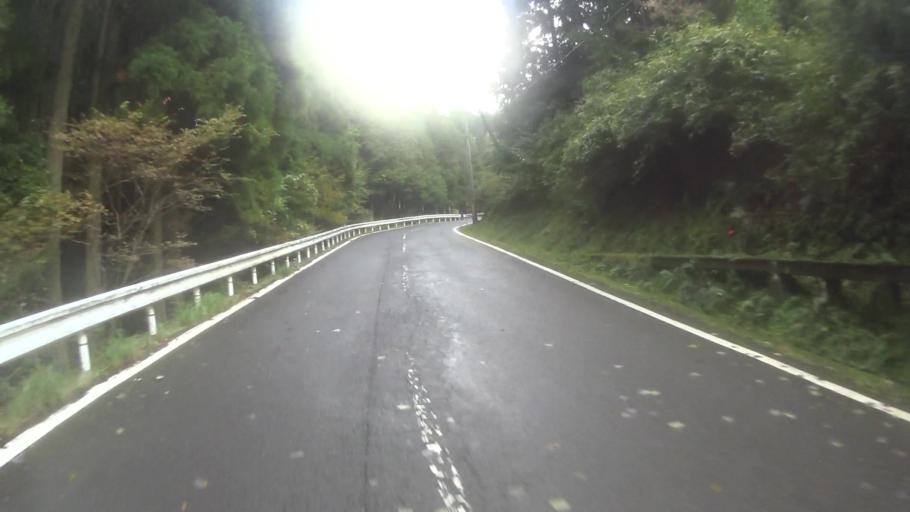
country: JP
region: Kyoto
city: Miyazu
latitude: 35.5019
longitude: 135.1384
